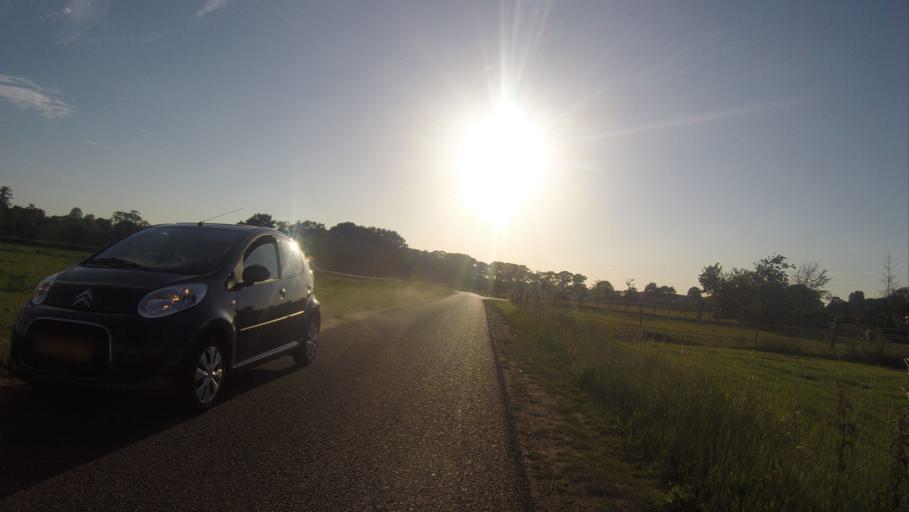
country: NL
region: Gelderland
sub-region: Gemeente Lochem
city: Lochem
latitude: 52.1242
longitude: 6.3901
